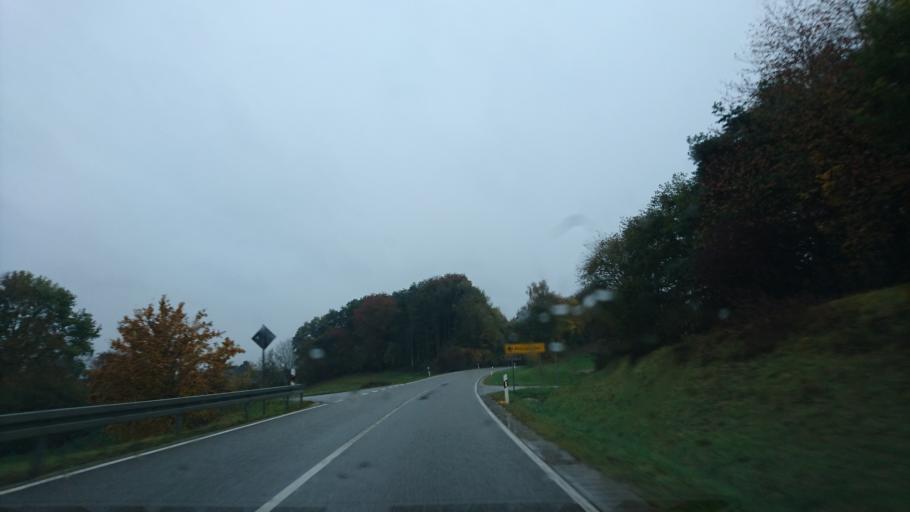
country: DE
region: Bavaria
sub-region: Swabia
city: Schiltberg
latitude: 48.4536
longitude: 11.2180
